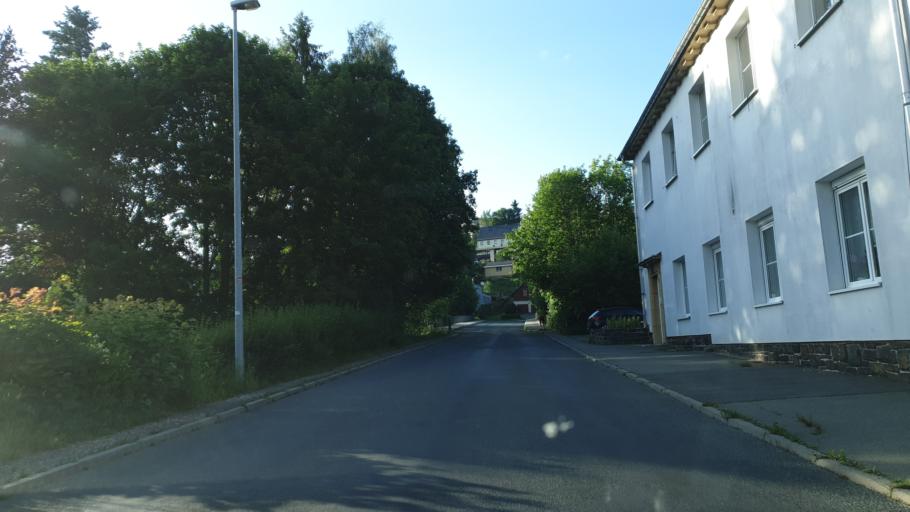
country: DE
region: Saxony
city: Klingenthal
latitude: 50.3562
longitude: 12.4537
